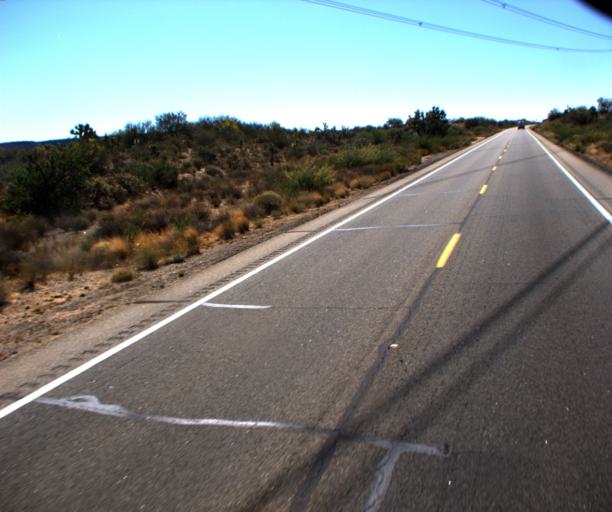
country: US
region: Arizona
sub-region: Yavapai County
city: Bagdad
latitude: 34.3388
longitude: -113.1513
